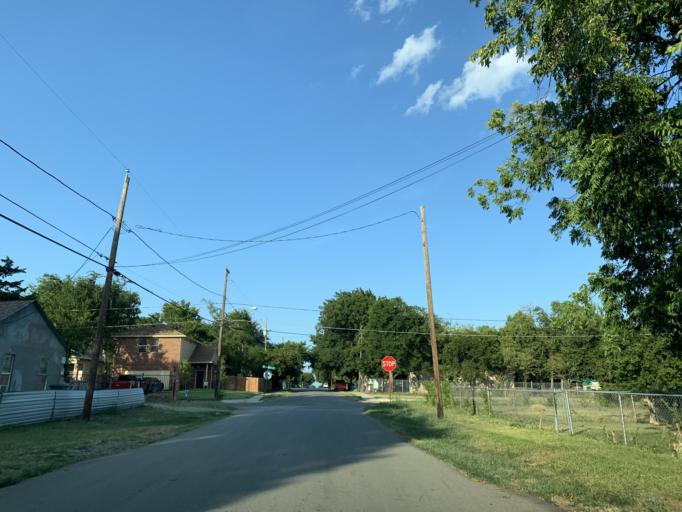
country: US
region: Texas
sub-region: Dallas County
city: Dallas
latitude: 32.7005
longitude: -96.7886
